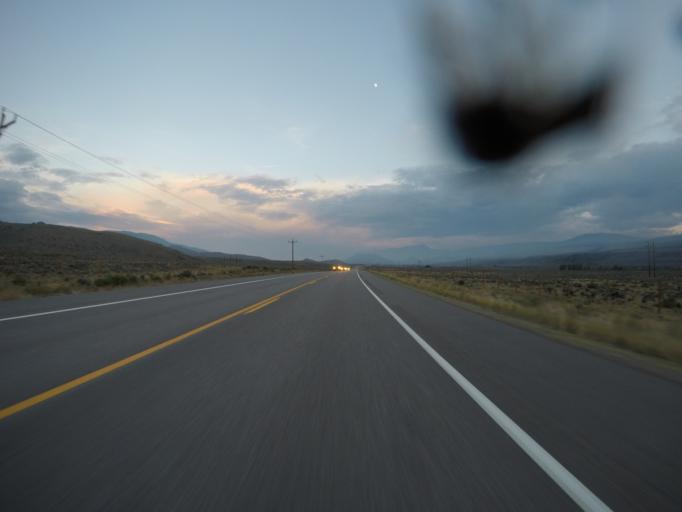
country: US
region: Colorado
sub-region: Grand County
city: Kremmling
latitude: 39.9779
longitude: -106.3538
